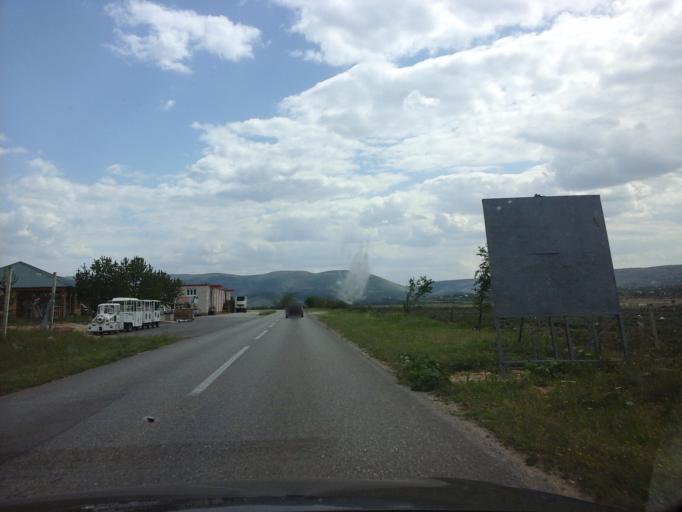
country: BA
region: Federation of Bosnia and Herzegovina
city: Blagaj
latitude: 43.2783
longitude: 17.8542
